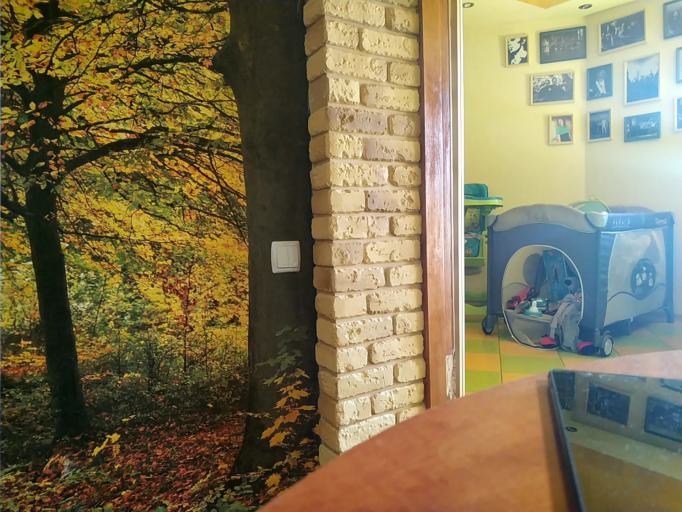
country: RU
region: Tverskaya
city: Vyshniy Volochek
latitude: 57.5213
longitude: 34.6272
